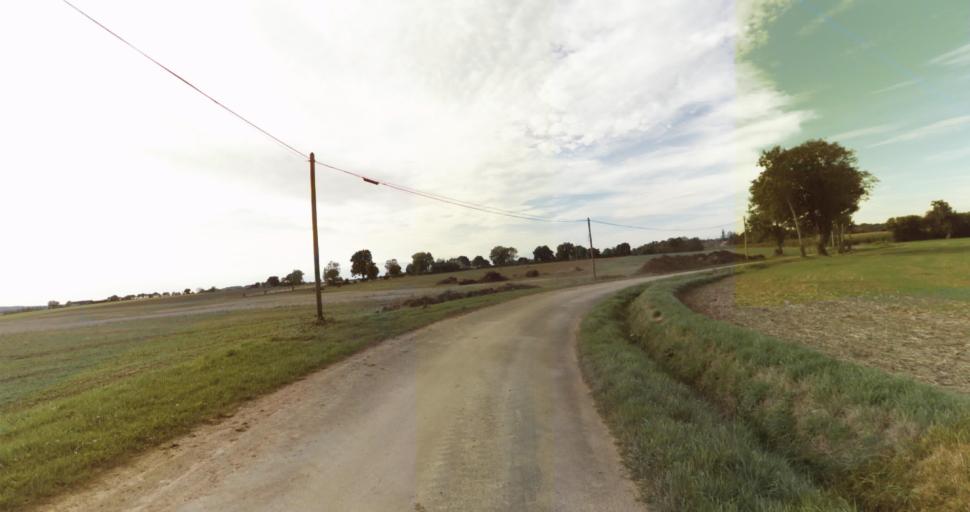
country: FR
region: Lower Normandy
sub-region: Departement de l'Orne
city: Gace
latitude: 48.7096
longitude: 0.2717
